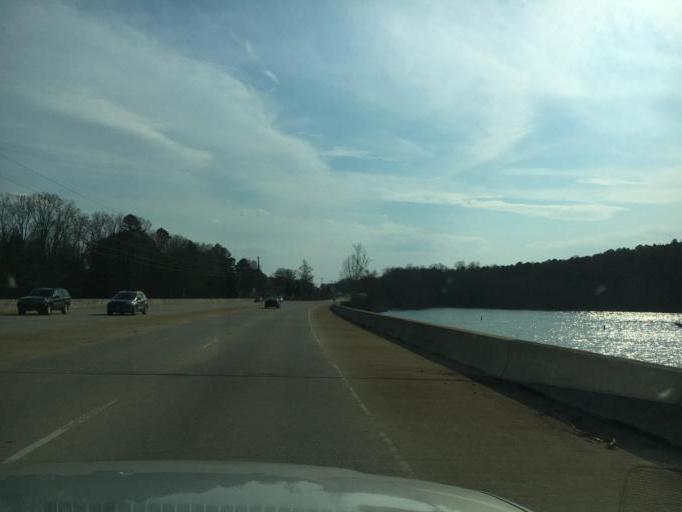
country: US
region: South Carolina
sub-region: Spartanburg County
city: Mayo
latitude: 35.0671
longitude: -81.8770
